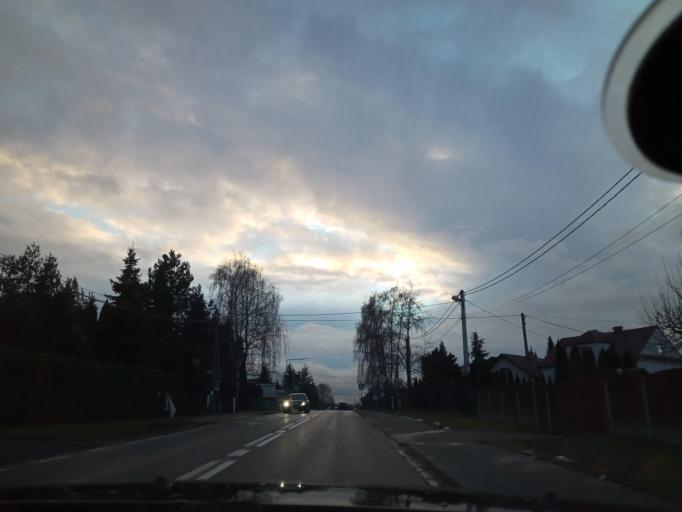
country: PL
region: Lesser Poland Voivodeship
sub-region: Powiat wielicki
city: Tomaszkowice
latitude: 49.9928
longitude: 20.0870
